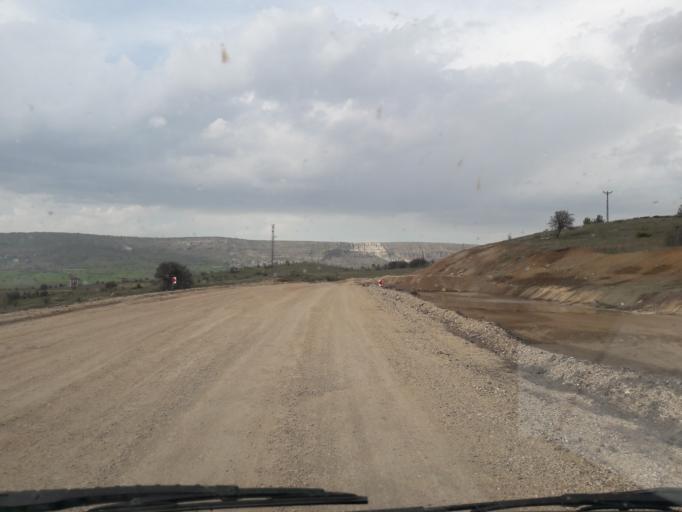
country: TR
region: Giresun
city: Alucra
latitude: 40.3172
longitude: 38.7724
